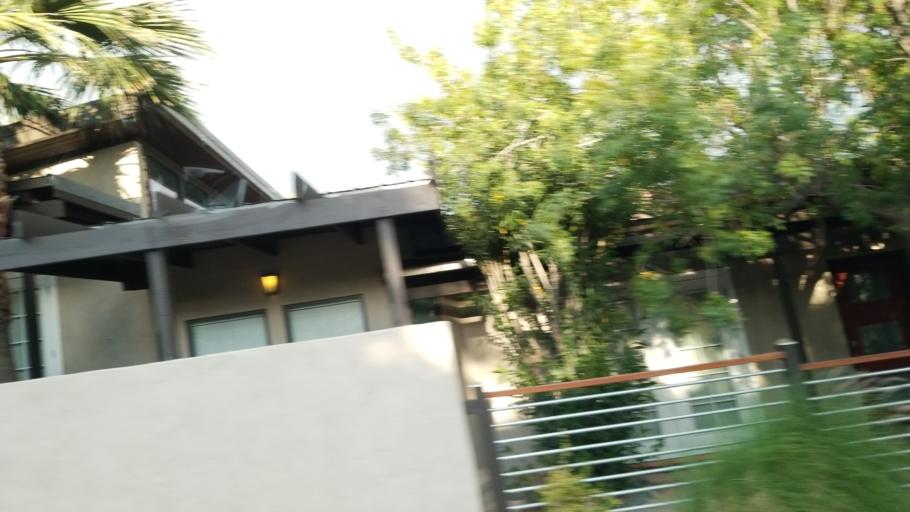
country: US
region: Arizona
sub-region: Maricopa County
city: Paradise Valley
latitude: 33.5906
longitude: -112.0521
